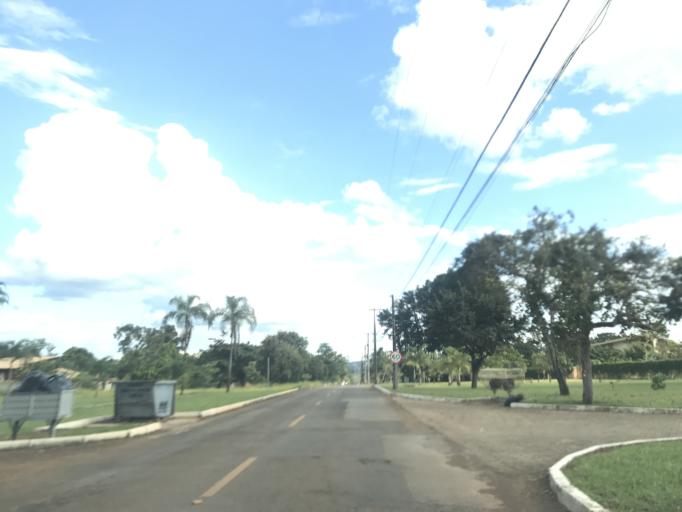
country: BR
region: Federal District
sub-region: Brasilia
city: Brasilia
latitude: -15.9076
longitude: -47.9405
